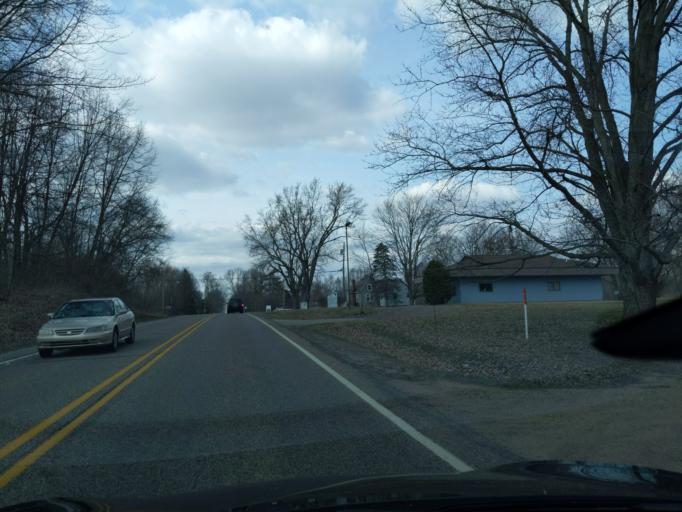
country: US
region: Michigan
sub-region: Jackson County
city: Jackson
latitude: 42.3089
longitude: -84.4136
